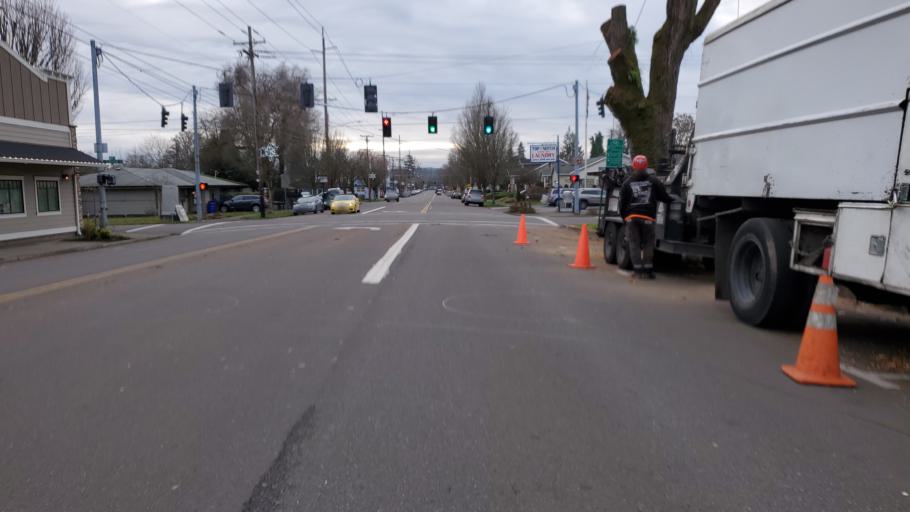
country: US
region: Oregon
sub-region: Clackamas County
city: Gladstone
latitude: 45.3825
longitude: -122.5961
